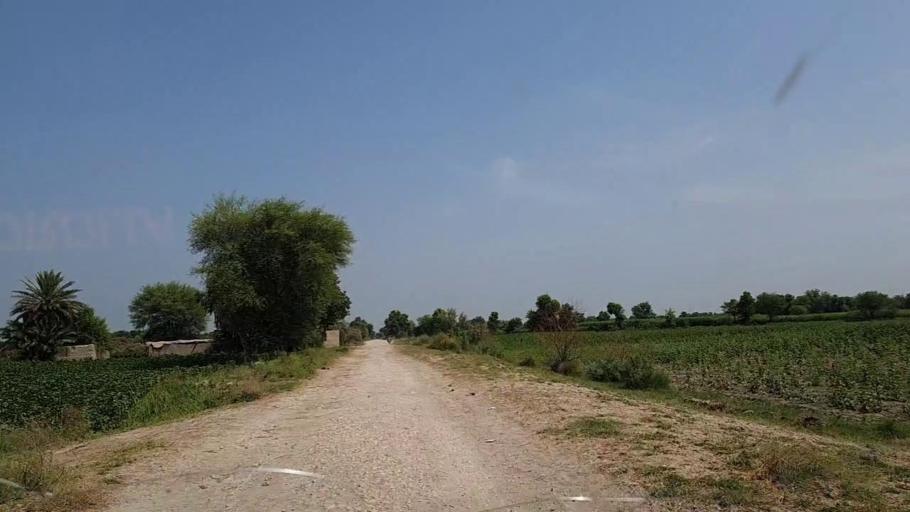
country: PK
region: Sindh
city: Adilpur
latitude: 27.8352
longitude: 69.2845
